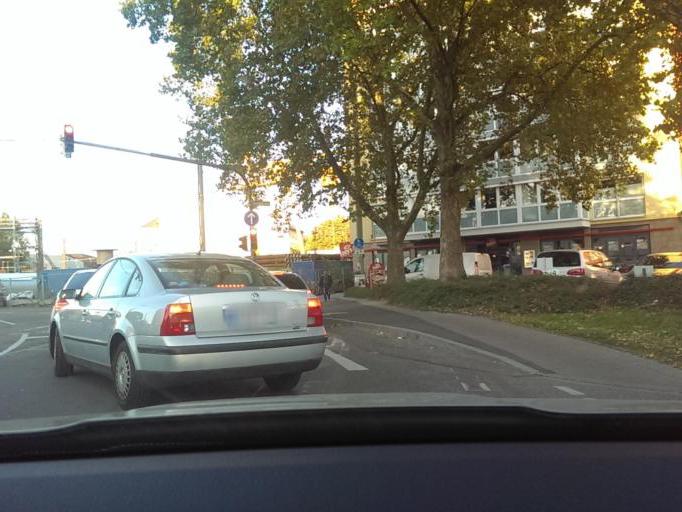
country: DE
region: Baden-Wuerttemberg
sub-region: Karlsruhe Region
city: Karlsruhe
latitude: 49.0086
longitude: 8.4170
